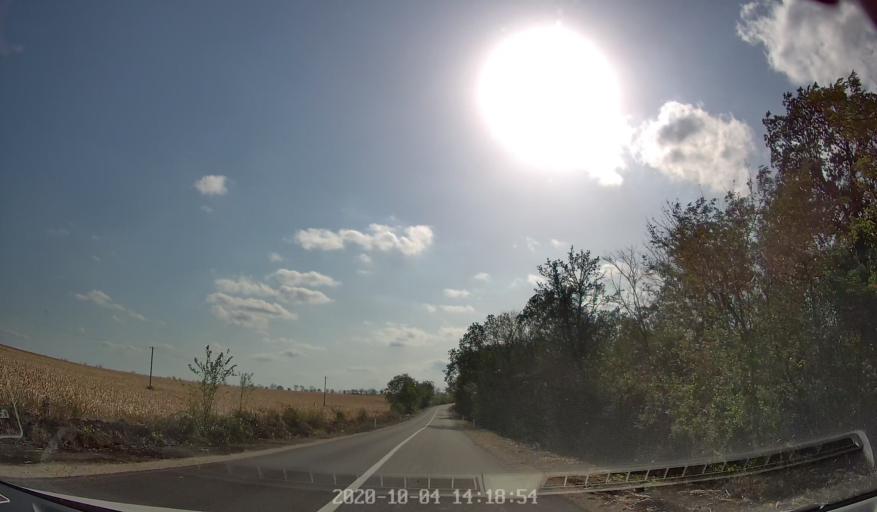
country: MD
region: Rezina
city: Saharna
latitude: 47.5956
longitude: 28.9768
